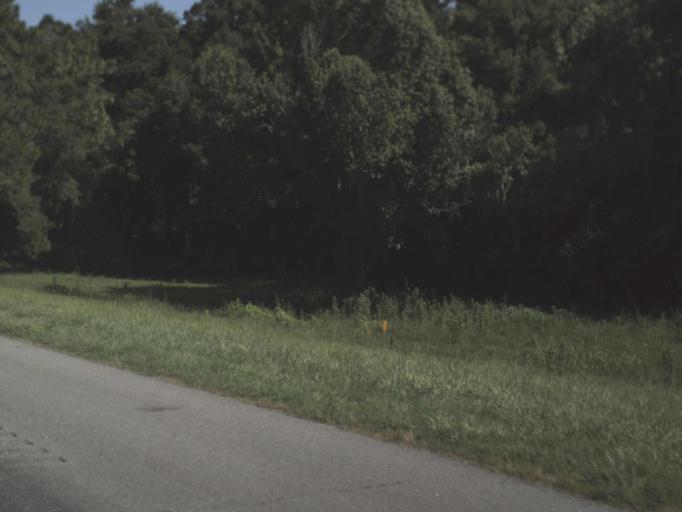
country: US
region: Florida
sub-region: Suwannee County
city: Live Oak
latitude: 30.3426
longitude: -82.9787
